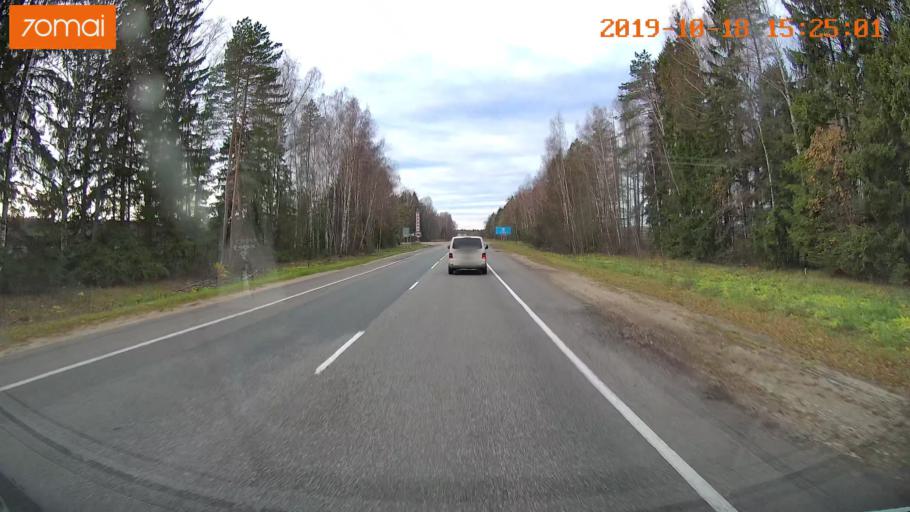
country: RU
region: Vladimir
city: Anopino
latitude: 55.7385
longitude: 40.7133
